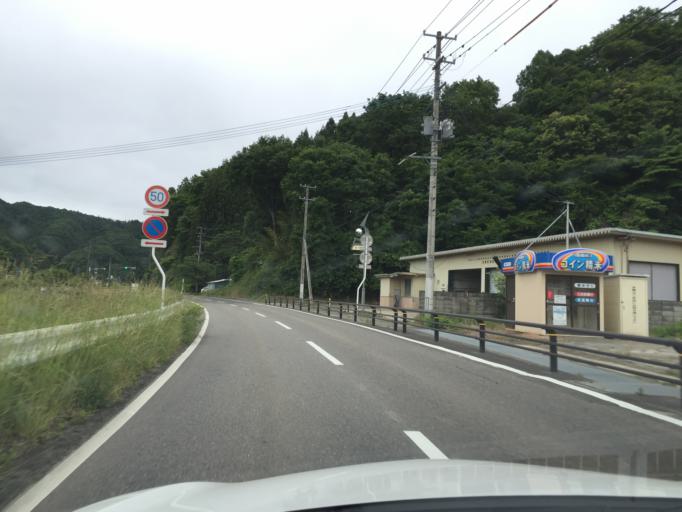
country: JP
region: Fukushima
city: Funehikimachi-funehiki
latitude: 37.3208
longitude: 140.6585
